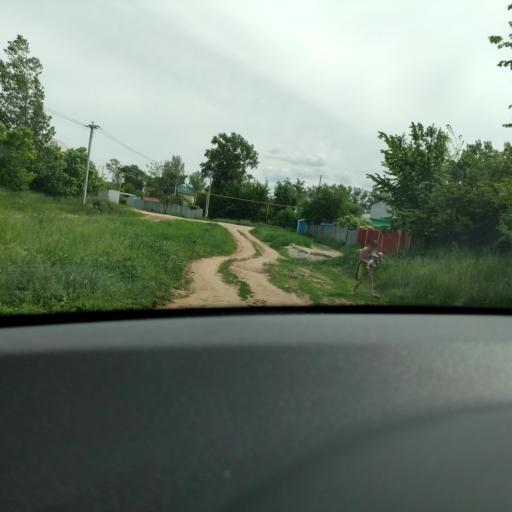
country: RU
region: Samara
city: Novokuybyshevsk
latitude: 53.1476
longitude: 50.0178
